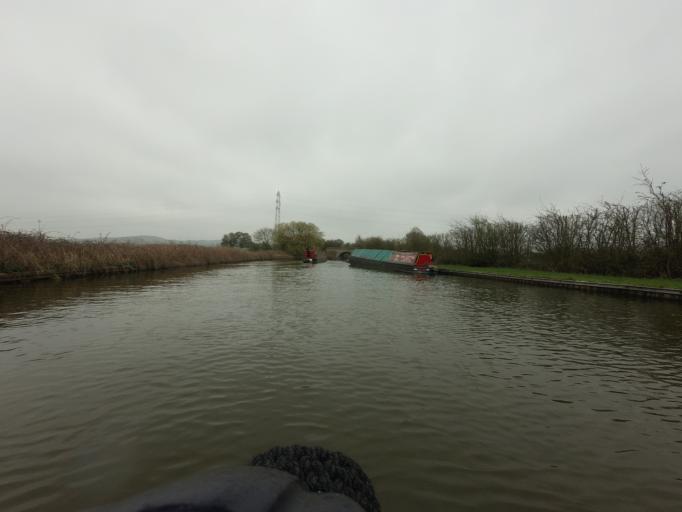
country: GB
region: England
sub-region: Buckinghamshire
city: Cheddington
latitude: 51.8563
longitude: -0.6465
